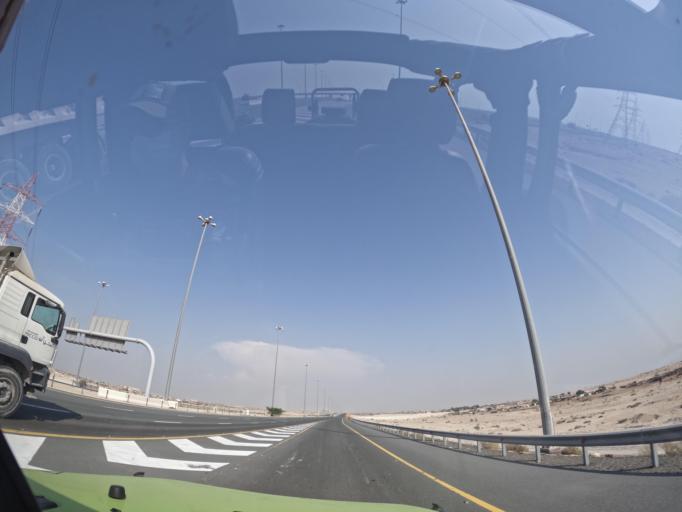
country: AE
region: Abu Dhabi
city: Abu Dhabi
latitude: 24.6778
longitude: 54.8286
